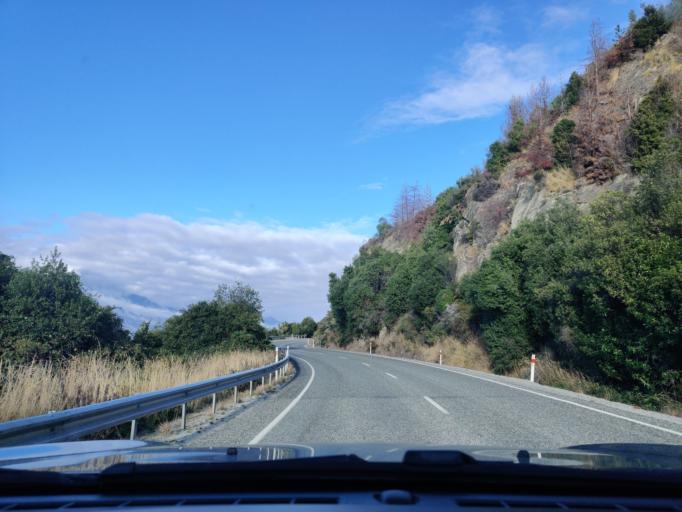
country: NZ
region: Otago
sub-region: Queenstown-Lakes District
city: Queenstown
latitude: -45.0532
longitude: 168.6184
